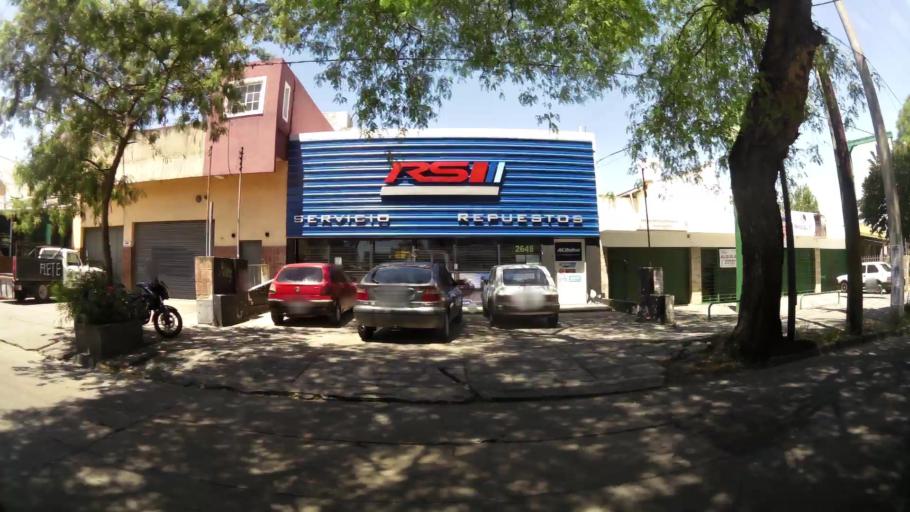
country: AR
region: Cordoba
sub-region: Departamento de Capital
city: Cordoba
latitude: -31.3799
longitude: -64.2074
